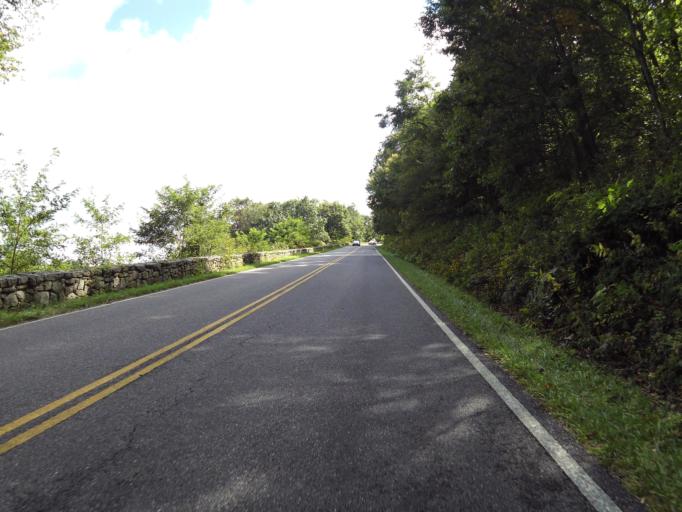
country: US
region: Virginia
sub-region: Page County
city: Luray
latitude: 38.6322
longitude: -78.3225
